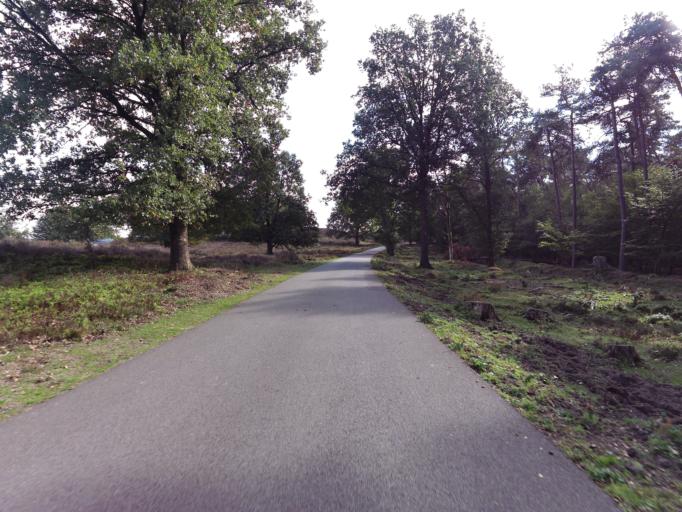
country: NL
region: Gelderland
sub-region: Gemeente Rheden
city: Rheden
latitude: 52.0245
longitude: 6.0076
